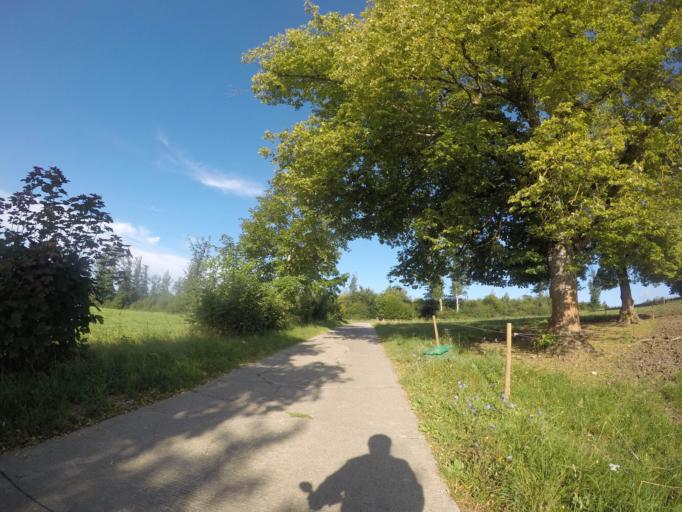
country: DE
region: Baden-Wuerttemberg
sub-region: Tuebingen Region
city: Schelklingen
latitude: 48.3932
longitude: 9.7325
